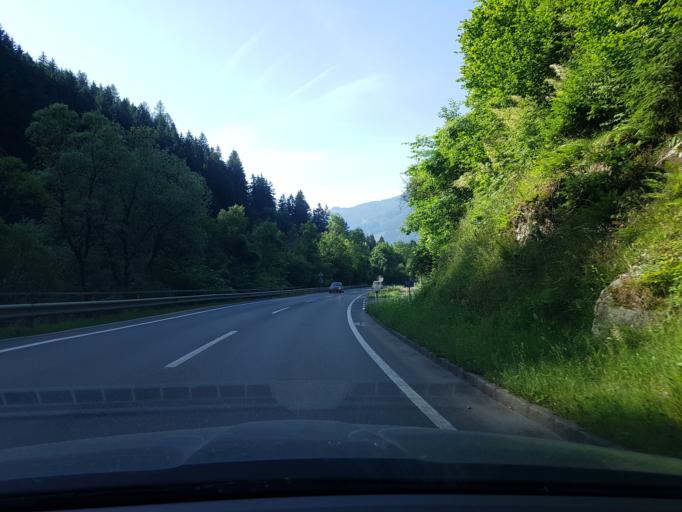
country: AT
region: Carinthia
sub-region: Politischer Bezirk Spittal an der Drau
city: Spittal an der Drau
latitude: 46.8084
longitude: 13.4959
